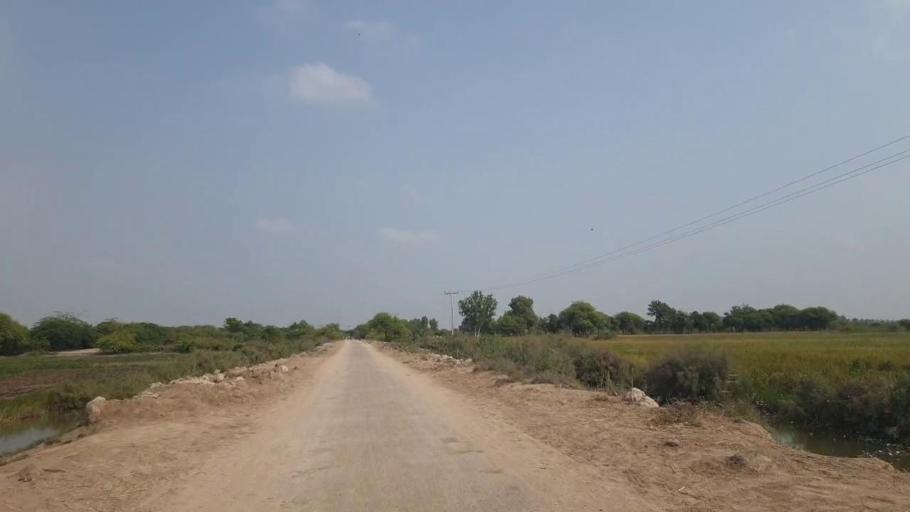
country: PK
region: Sindh
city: Badin
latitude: 24.5478
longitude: 68.7233
